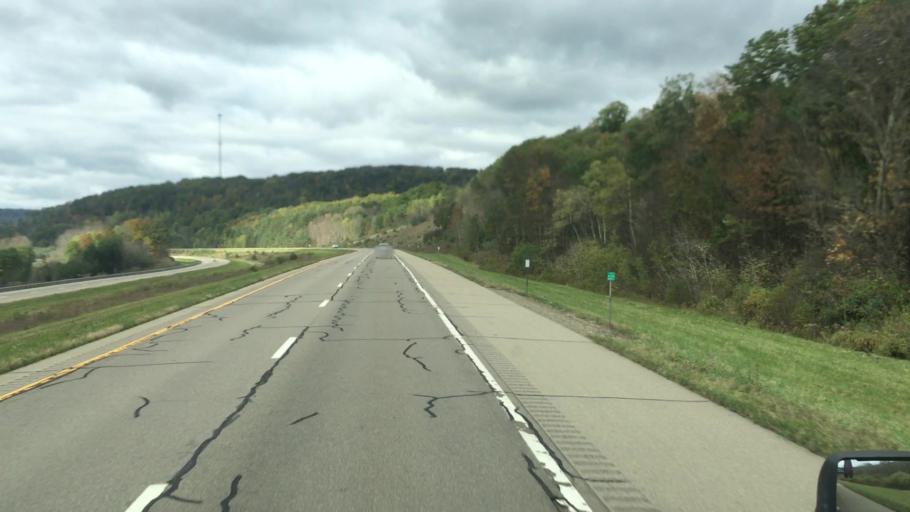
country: US
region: New York
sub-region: Allegany County
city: Cuba
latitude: 42.2236
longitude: -78.2417
